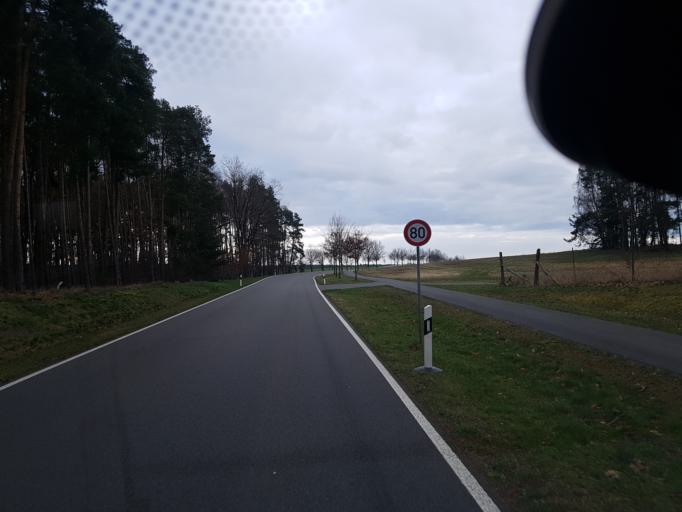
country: DE
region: Brandenburg
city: Gross Lindow
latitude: 52.1574
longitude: 14.5150
